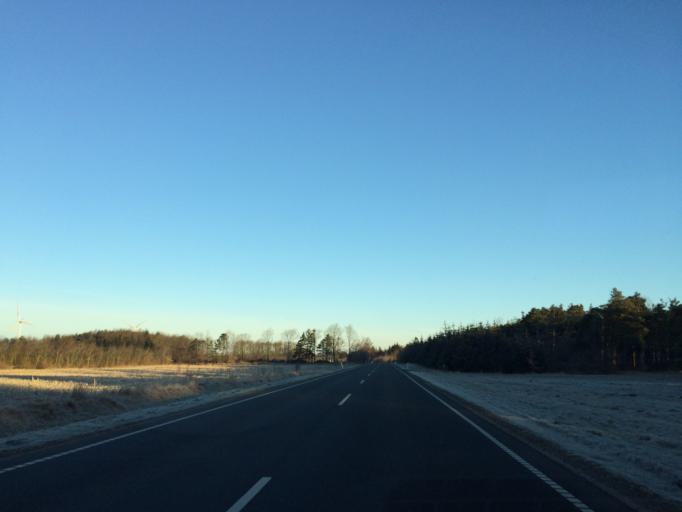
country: DK
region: Central Jutland
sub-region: Holstebro Kommune
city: Ulfborg
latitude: 56.3629
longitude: 8.3359
